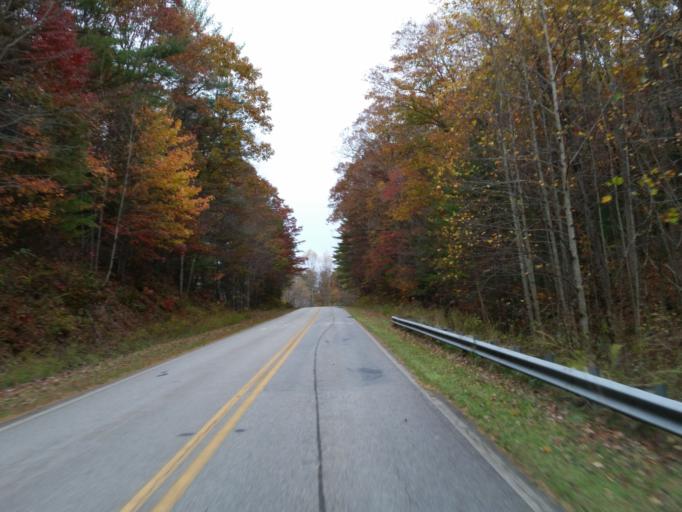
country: US
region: Georgia
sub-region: Fannin County
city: Blue Ridge
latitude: 34.6892
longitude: -84.2590
